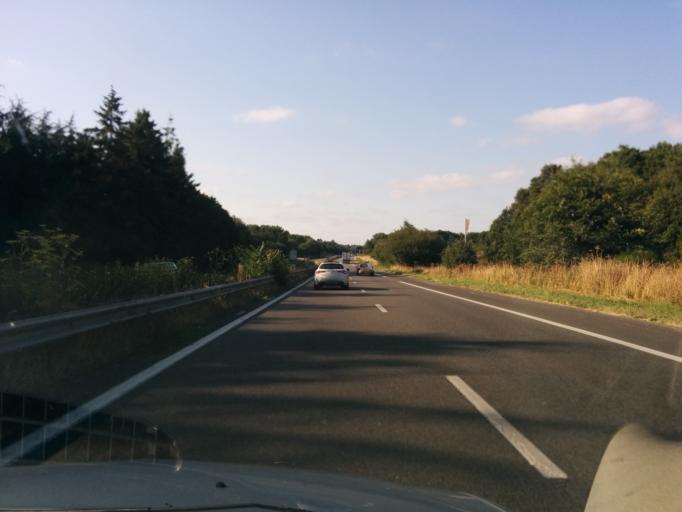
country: FR
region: Pays de la Loire
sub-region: Departement de la Loire-Atlantique
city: Carquefou
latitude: 47.2797
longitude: -1.4796
